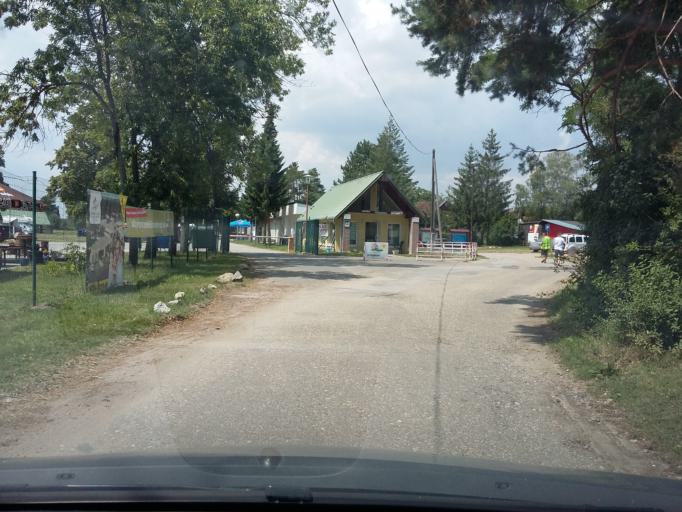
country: AT
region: Lower Austria
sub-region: Politischer Bezirk Ganserndorf
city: Drosing
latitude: 48.4911
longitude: 16.9564
